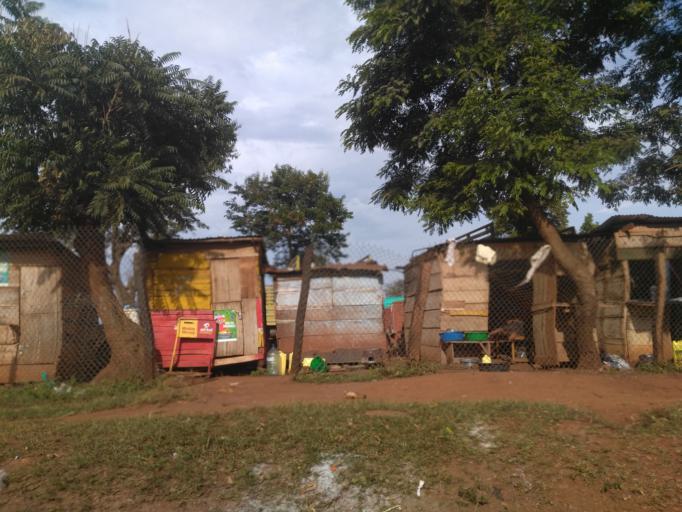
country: UG
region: Eastern Region
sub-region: Jinja District
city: Jinja
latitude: 0.4169
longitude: 33.2142
